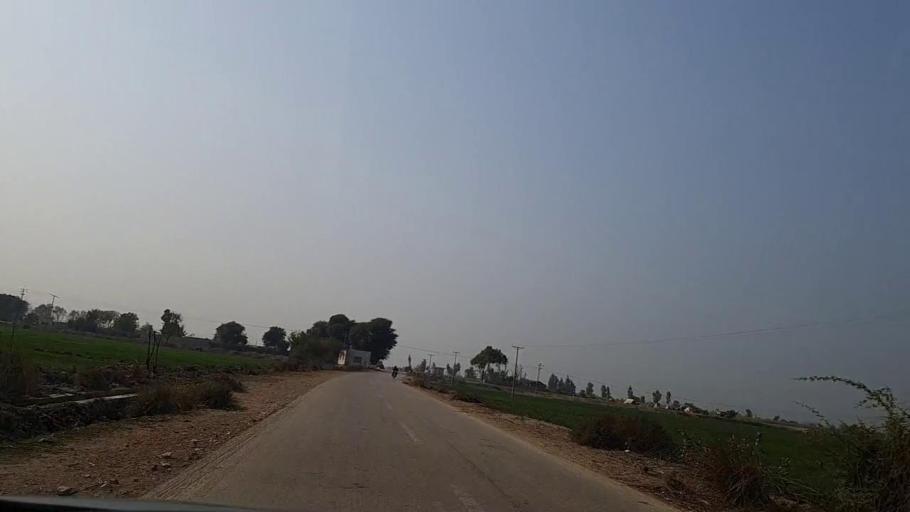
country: PK
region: Sindh
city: Sakrand
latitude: 26.1373
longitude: 68.1754
